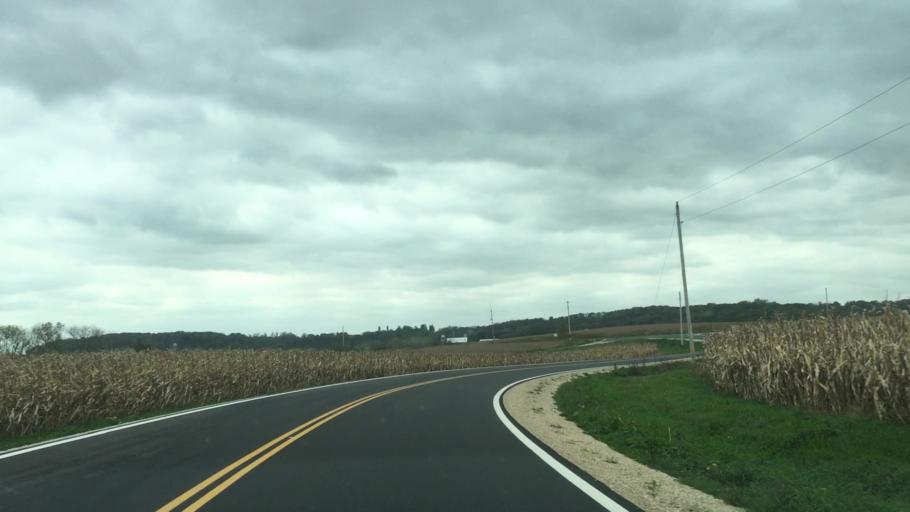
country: US
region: Minnesota
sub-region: Fillmore County
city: Preston
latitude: 43.7548
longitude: -92.0204
